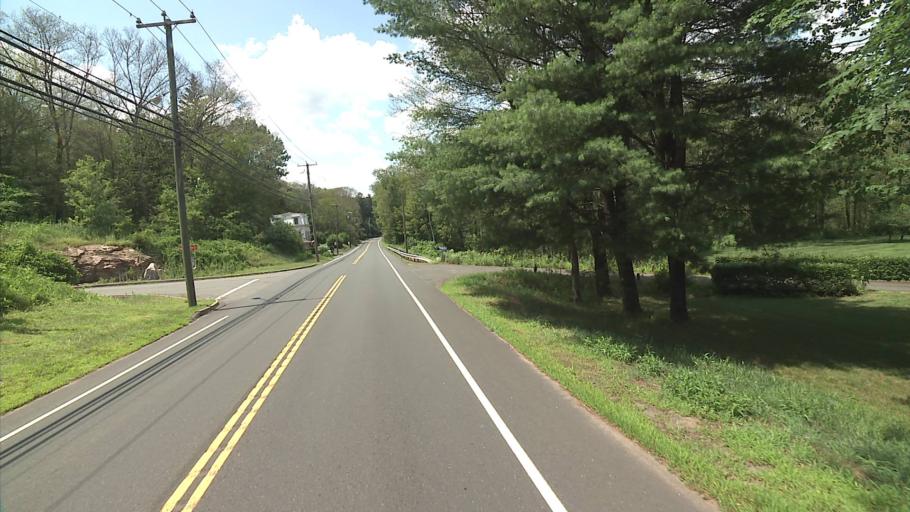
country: US
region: Connecticut
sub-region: Middlesex County
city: Higganum
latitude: 41.4973
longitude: -72.5460
